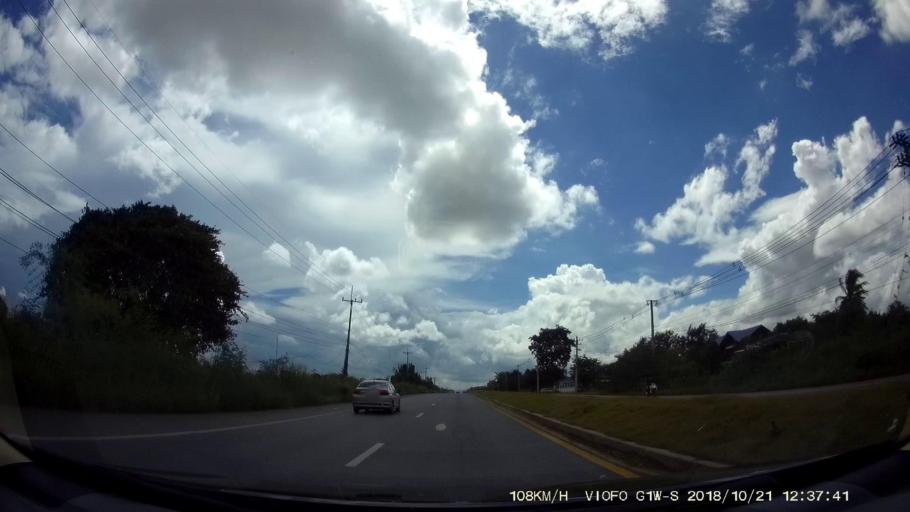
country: TH
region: Nakhon Ratchasima
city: Dan Khun Thot
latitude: 15.0654
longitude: 101.7101
